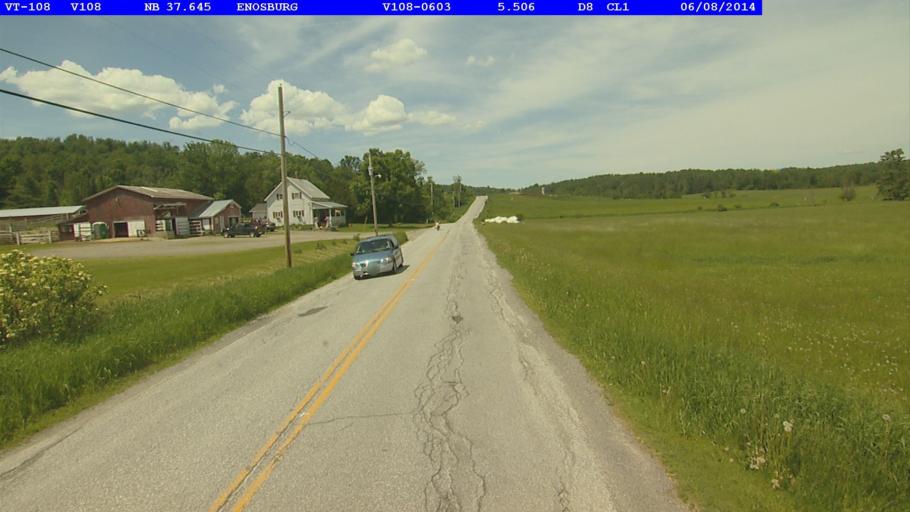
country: US
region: Vermont
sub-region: Franklin County
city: Enosburg Falls
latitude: 44.9196
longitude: -72.8068
